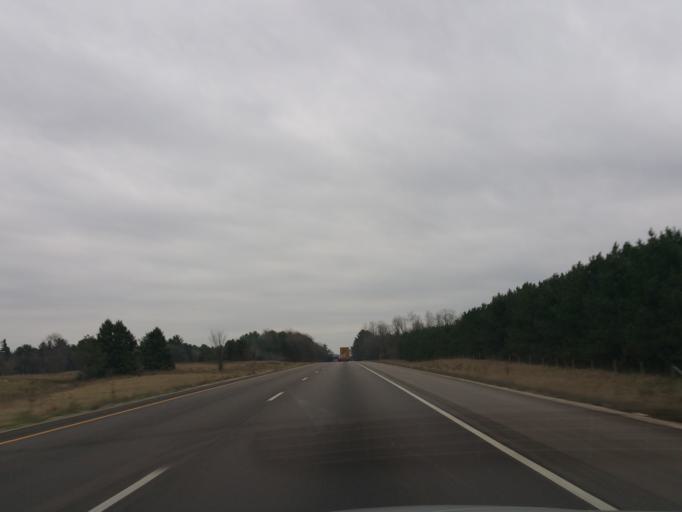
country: US
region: Wisconsin
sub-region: Eau Claire County
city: Altoona
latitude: 44.7543
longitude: -91.3921
